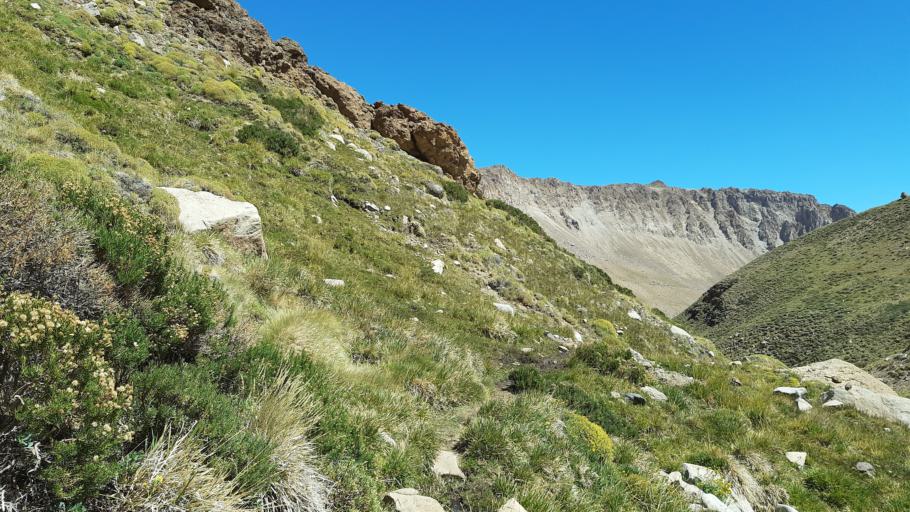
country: AR
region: Neuquen
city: Las Ovejas
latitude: -36.6787
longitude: -70.4936
